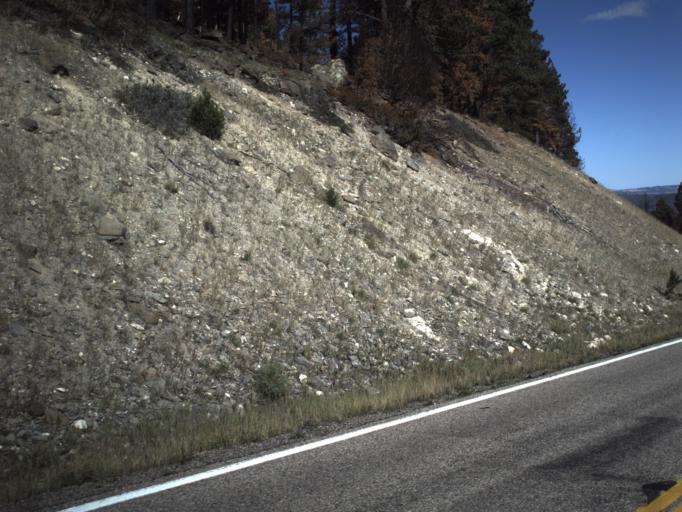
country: US
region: Utah
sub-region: Iron County
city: Parowan
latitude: 37.6510
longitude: -112.6951
